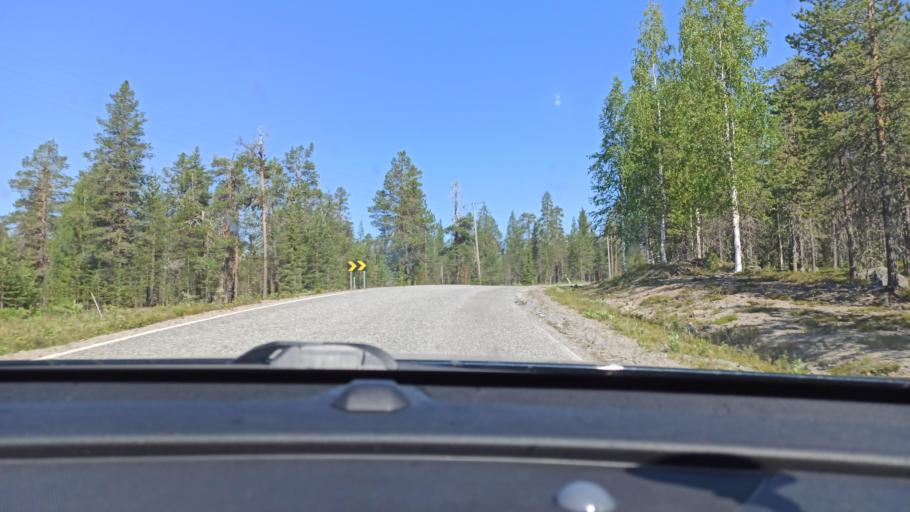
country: FI
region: Lapland
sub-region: Tunturi-Lappi
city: Kolari
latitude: 67.6369
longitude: 24.1567
